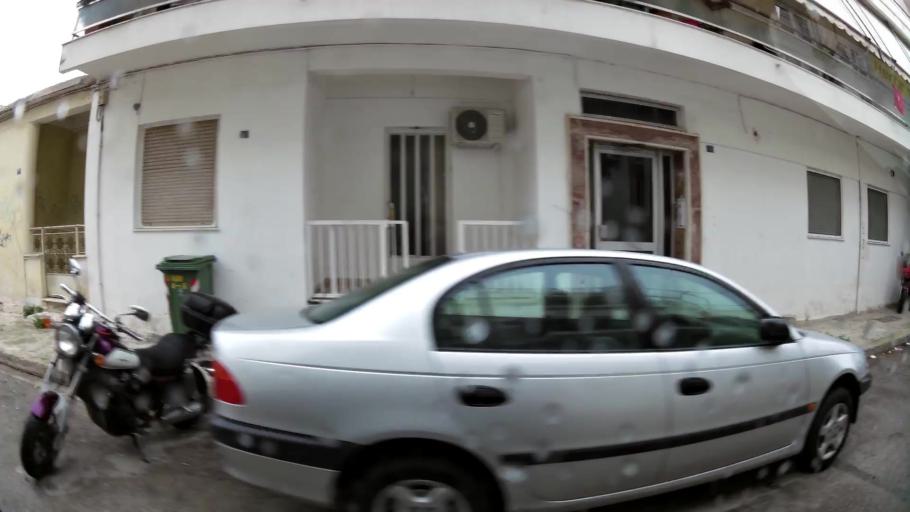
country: GR
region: Attica
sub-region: Nomos Piraios
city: Korydallos
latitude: 37.9849
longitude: 23.6393
